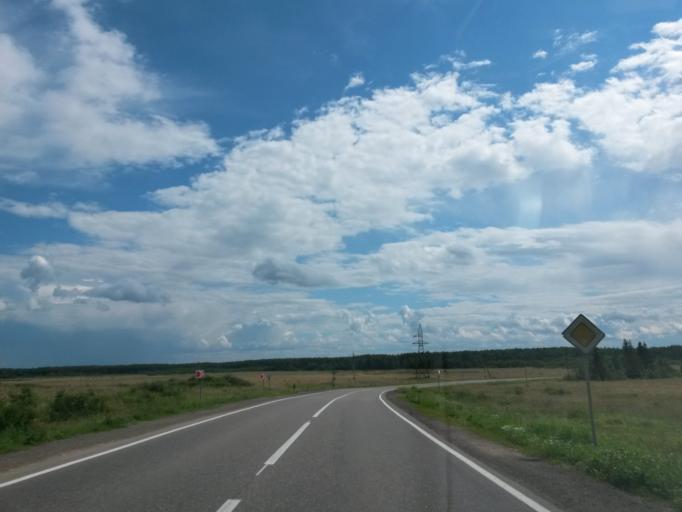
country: RU
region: Jaroslavl
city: Gavrilov-Yam
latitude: 57.3042
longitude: 39.9455
